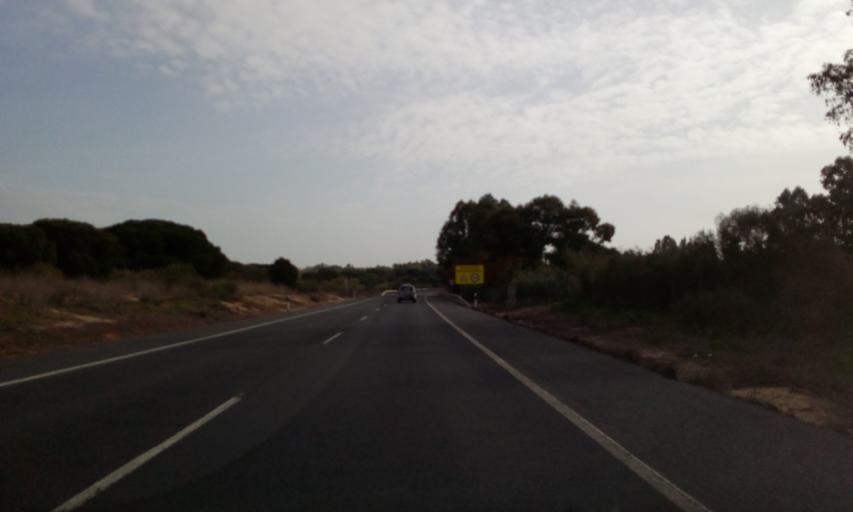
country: ES
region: Andalusia
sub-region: Provincia de Huelva
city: Palos de la Frontera
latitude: 37.1679
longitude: -6.8922
